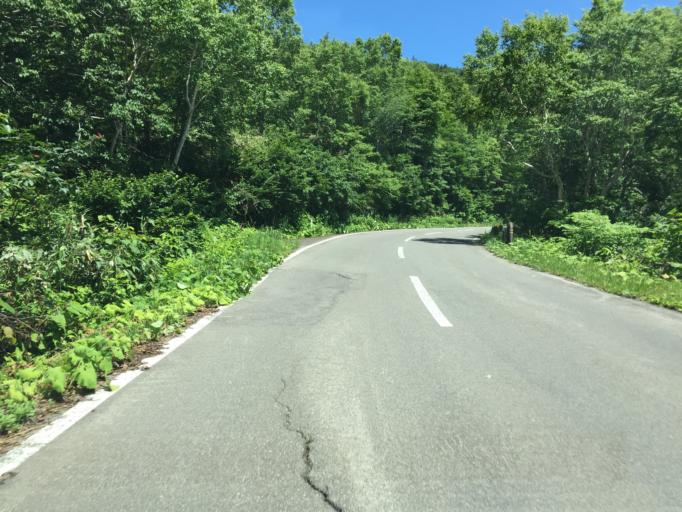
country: JP
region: Fukushima
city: Inawashiro
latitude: 37.6876
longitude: 140.2330
